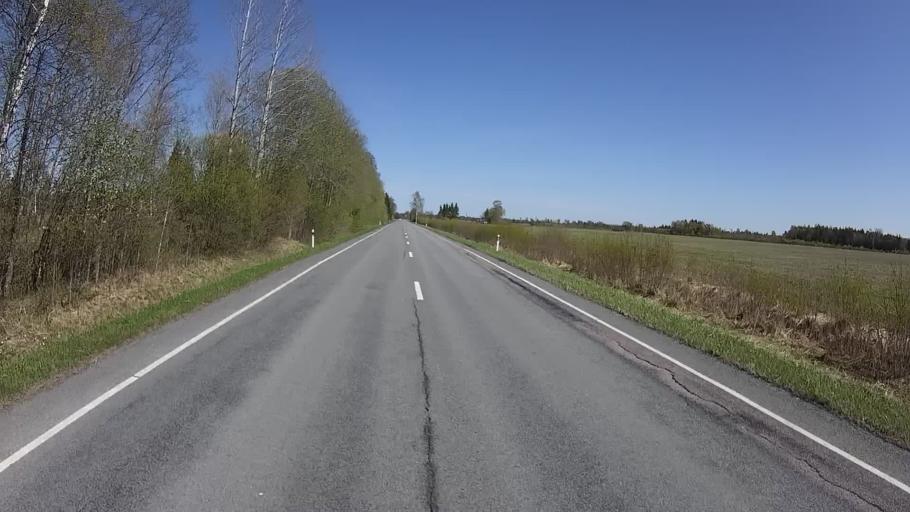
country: EE
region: Raplamaa
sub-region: Jaervakandi vald
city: Jarvakandi
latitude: 58.8314
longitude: 24.7973
